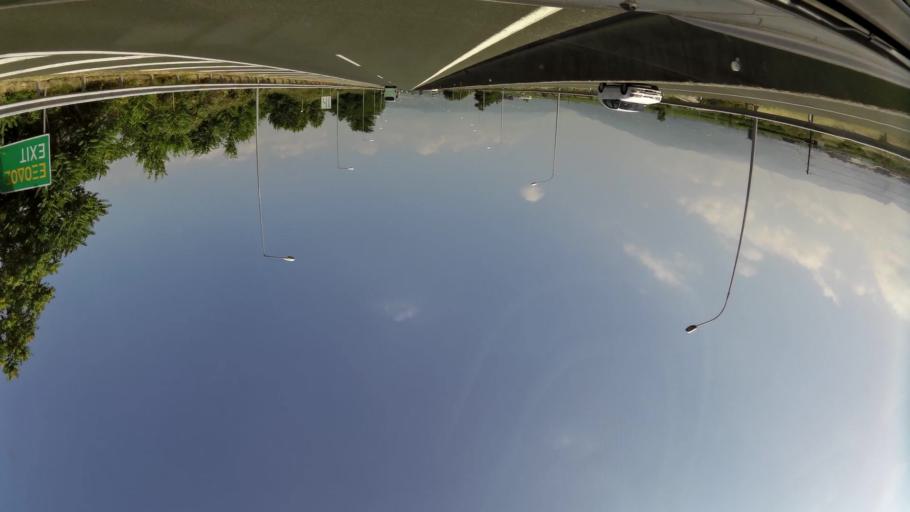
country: GR
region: Central Macedonia
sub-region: Nomos Imathias
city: Kouloura
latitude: 40.5417
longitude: 22.3175
